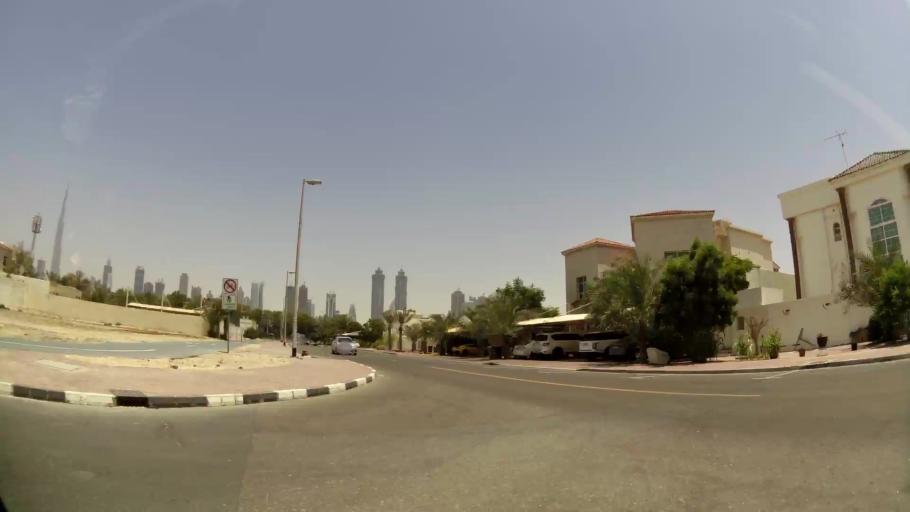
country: AE
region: Dubai
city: Dubai
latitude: 25.1978
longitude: 55.2453
